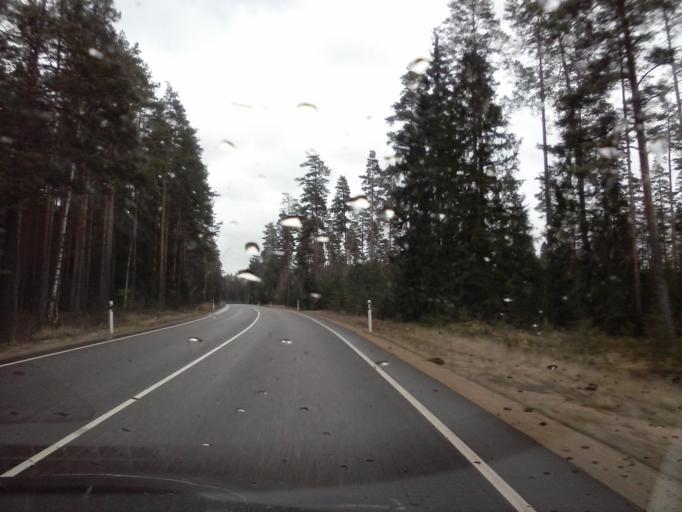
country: EE
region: Polvamaa
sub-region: Raepina vald
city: Rapina
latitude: 57.9753
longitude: 27.3031
